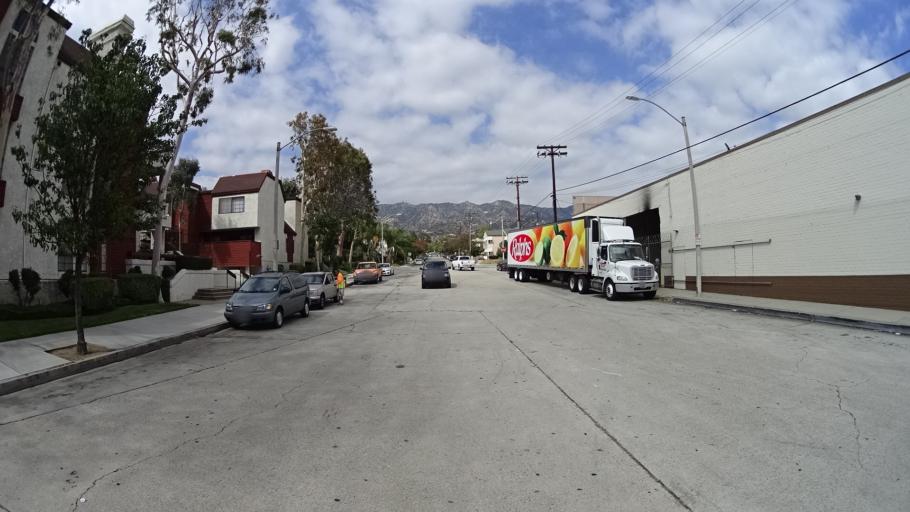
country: US
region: California
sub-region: Los Angeles County
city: Burbank
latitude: 34.1893
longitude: -118.3187
